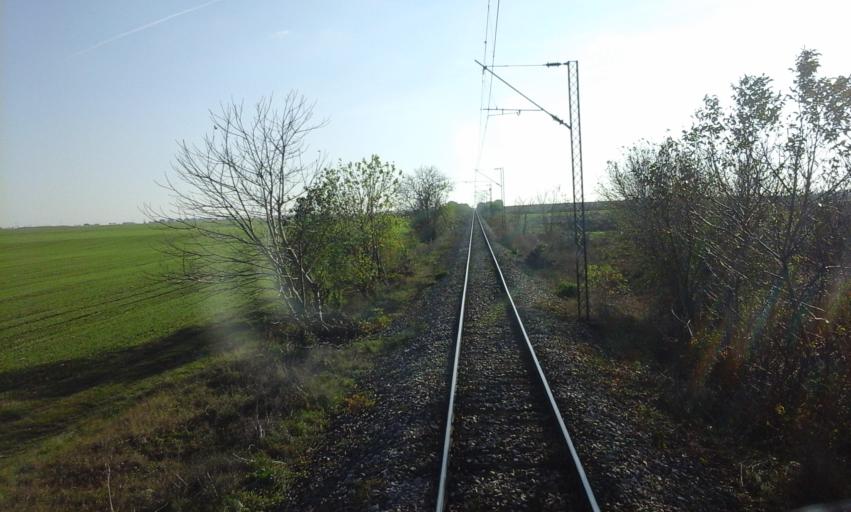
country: RS
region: Autonomna Pokrajina Vojvodina
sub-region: Severnobacki Okrug
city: Backa Topola
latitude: 45.7724
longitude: 19.6481
